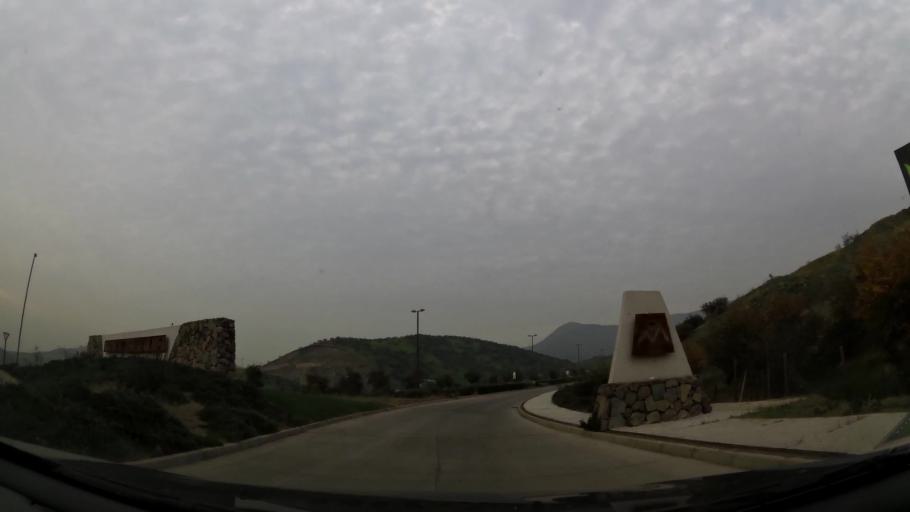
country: CL
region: Santiago Metropolitan
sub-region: Provincia de Chacabuco
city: Chicureo Abajo
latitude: -33.3226
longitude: -70.6283
